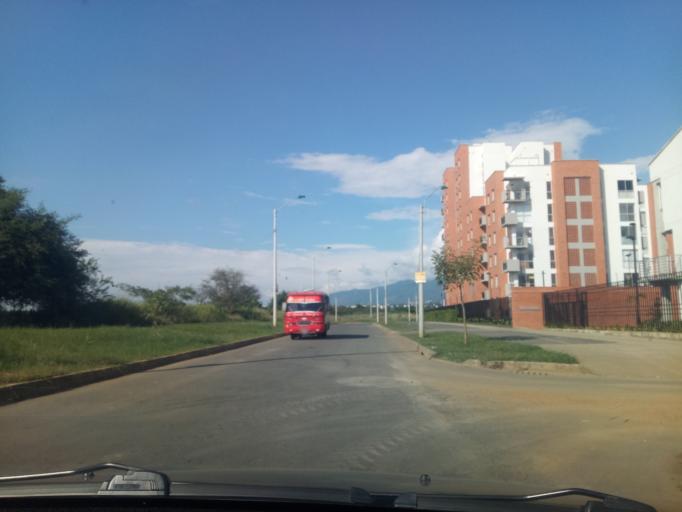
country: CO
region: Valle del Cauca
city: Cali
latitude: 3.3659
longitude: -76.5076
